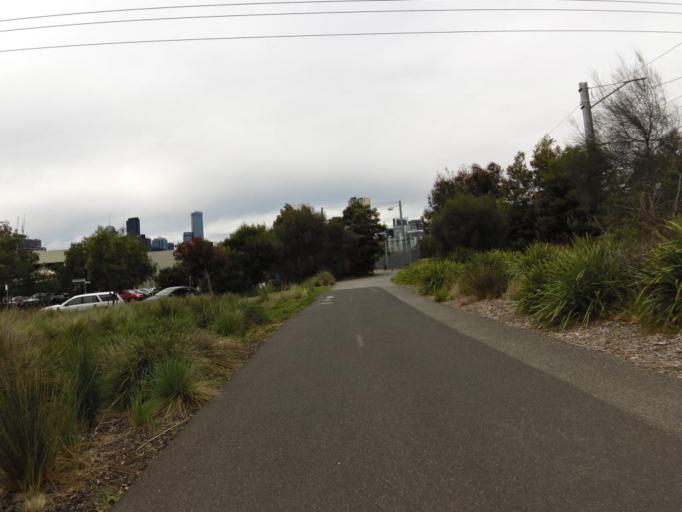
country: AU
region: Victoria
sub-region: Port Phillip
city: Port Melbourne
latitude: -37.8315
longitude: 144.9462
